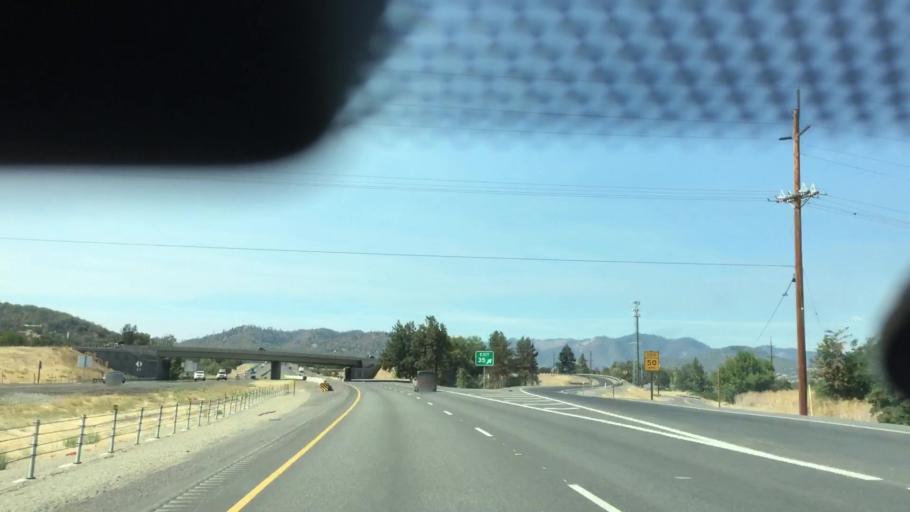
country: US
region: Oregon
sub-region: Jackson County
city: Central Point
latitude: 42.4046
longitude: -122.9395
